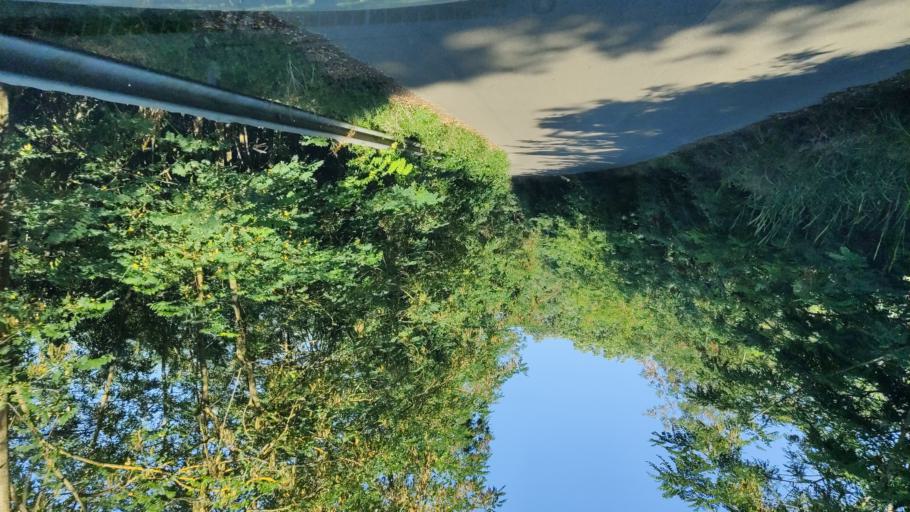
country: IT
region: Latium
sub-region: Provincia di Viterbo
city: Orte
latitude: 42.4699
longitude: 12.3731
